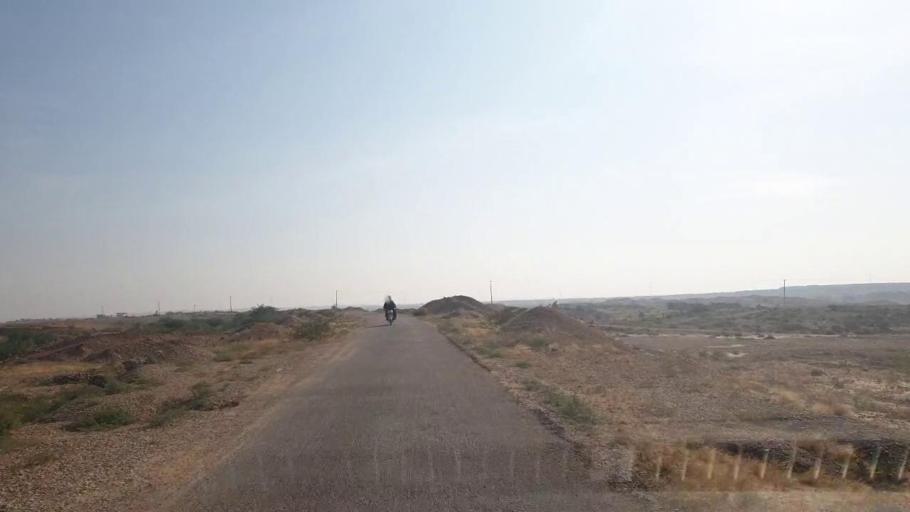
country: PK
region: Sindh
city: Matiari
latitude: 25.6228
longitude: 68.3091
